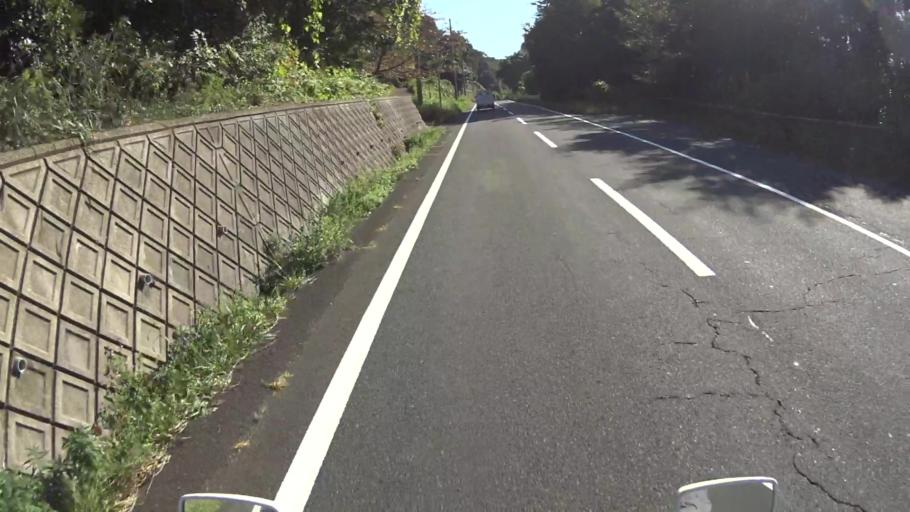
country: JP
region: Kyoto
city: Miyazu
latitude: 35.7059
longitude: 135.0692
